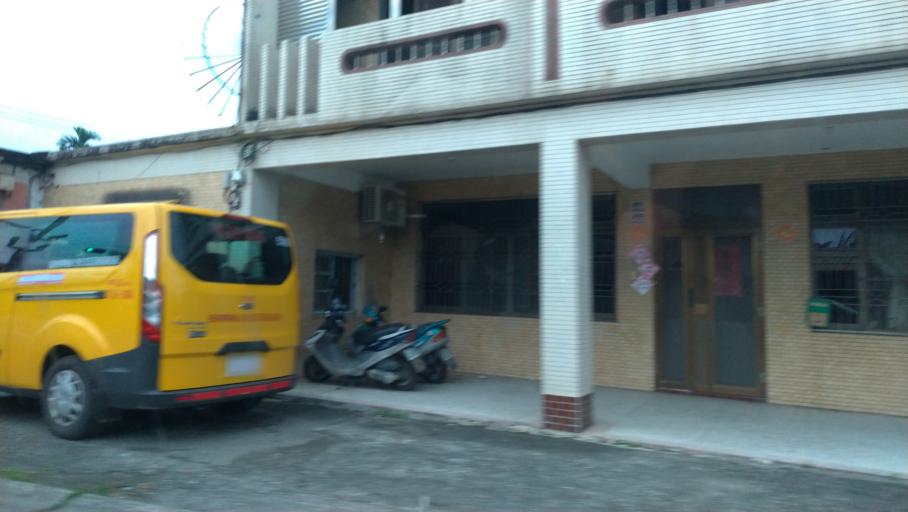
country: TW
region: Taiwan
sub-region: Yilan
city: Yilan
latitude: 24.8407
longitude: 121.8060
